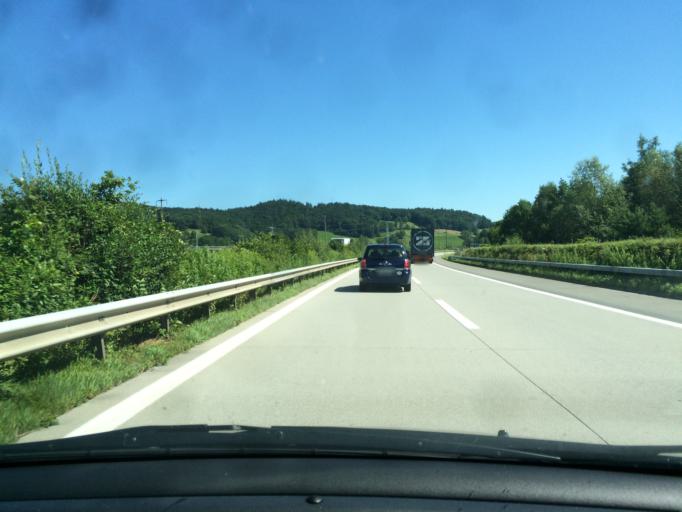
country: CH
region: Saint Gallen
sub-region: Wahlkreis Rheintal
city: Ruthi
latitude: 47.2960
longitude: 9.5529
